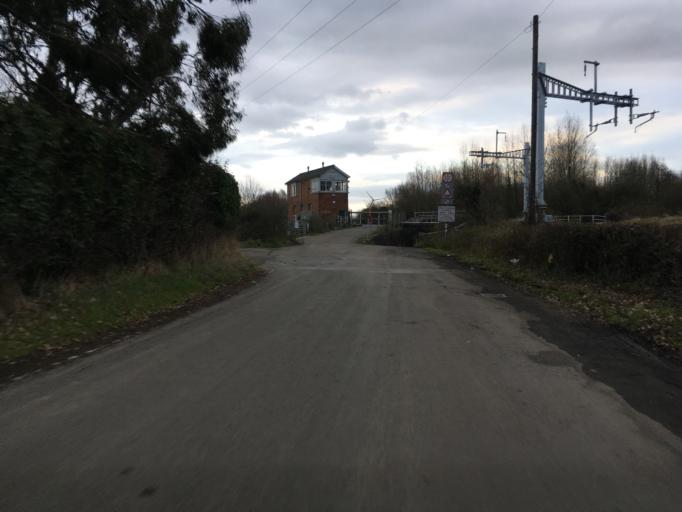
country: GB
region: Wales
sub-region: Newport
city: Bishton
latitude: 51.5802
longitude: -2.8747
